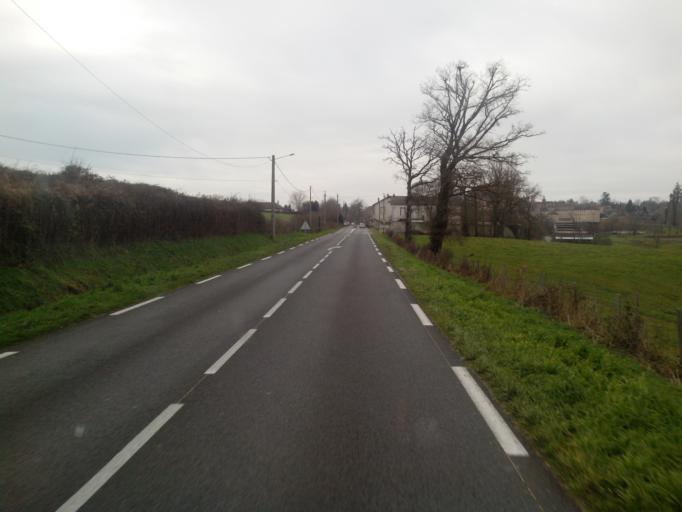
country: FR
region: Limousin
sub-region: Departement de la Haute-Vienne
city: Magnac-Laval
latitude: 46.2114
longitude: 1.1764
